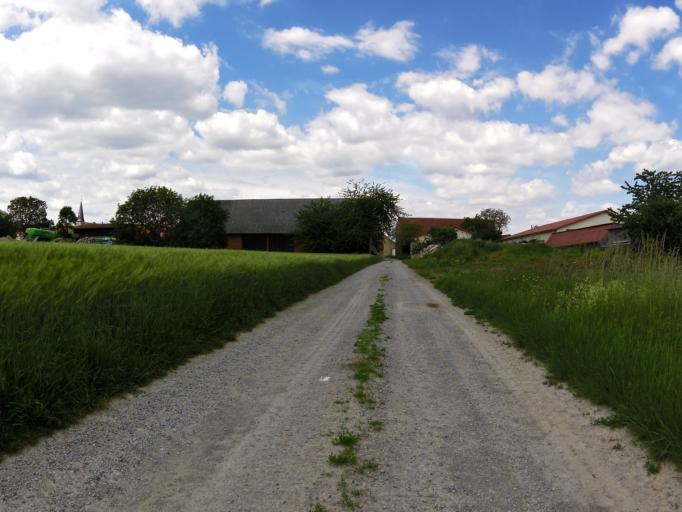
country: DE
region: Bavaria
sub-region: Regierungsbezirk Unterfranken
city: Biebelried
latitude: 49.7423
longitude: 10.0672
